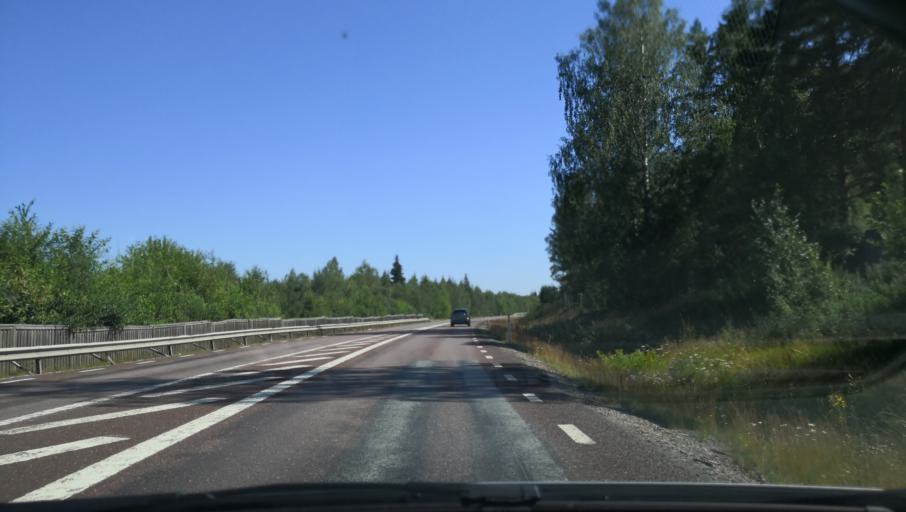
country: SE
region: Gaevleborg
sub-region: Ovanakers Kommun
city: Alfta
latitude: 61.3438
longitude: 16.0156
